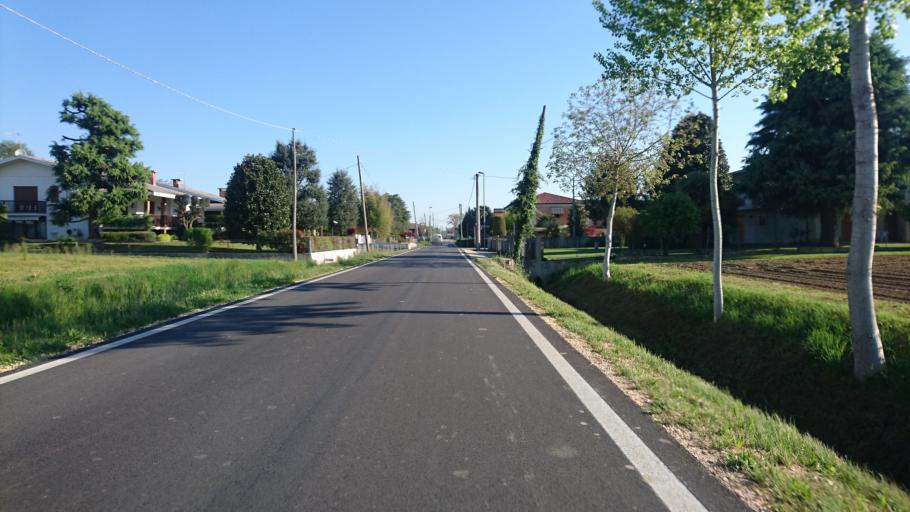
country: IT
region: Veneto
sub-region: Provincia di Padova
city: Massanzago-Ca' Baglioni-San Dono
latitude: 45.5396
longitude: 12.0055
